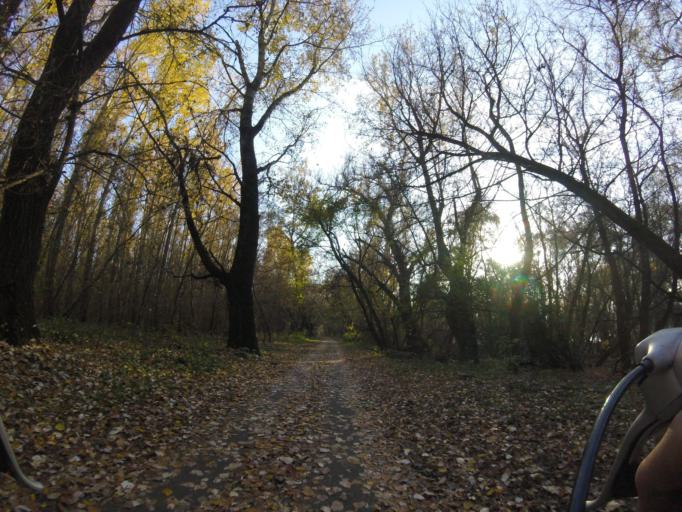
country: HU
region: Pest
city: Szodliget
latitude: 47.7487
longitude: 19.1368
